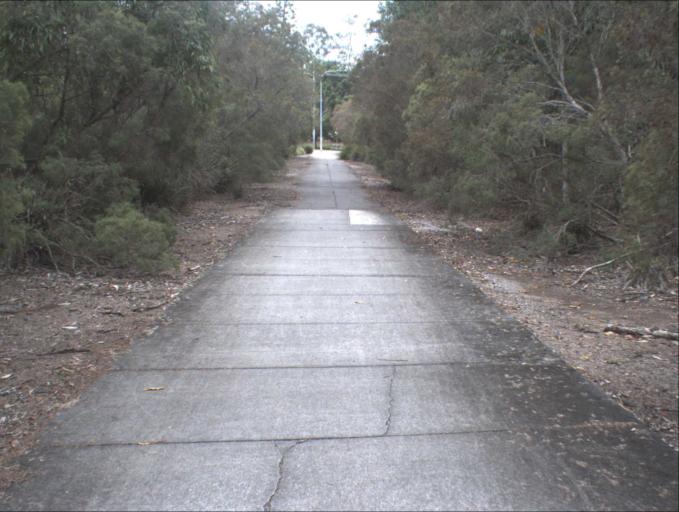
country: AU
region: Queensland
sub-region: Gold Coast
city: Yatala
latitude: -27.7149
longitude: 153.2103
